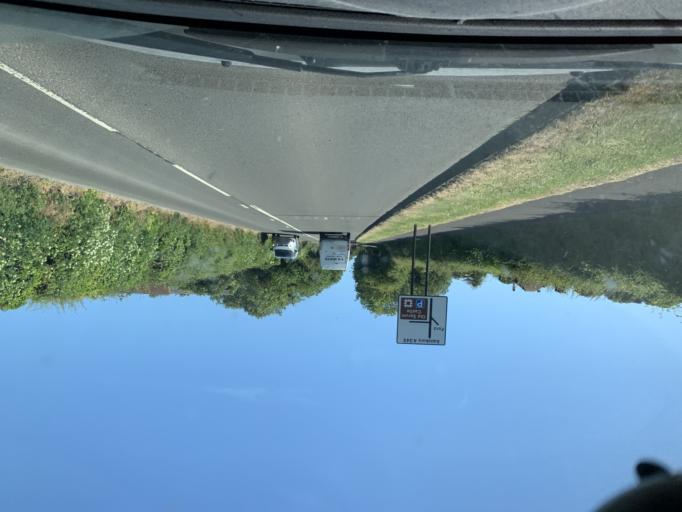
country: GB
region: England
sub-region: Wiltshire
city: Salisbury
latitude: 51.0944
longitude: -1.7992
